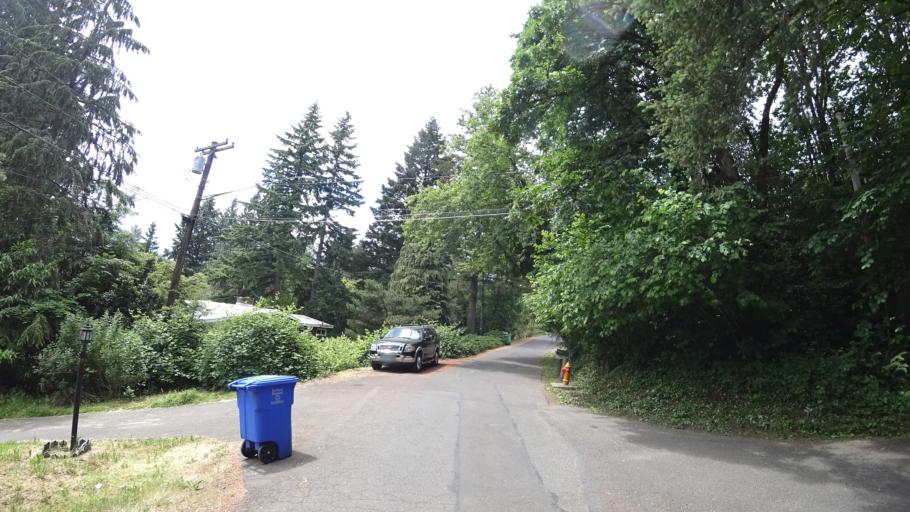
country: US
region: Oregon
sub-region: Clackamas County
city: Lake Oswego
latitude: 45.4496
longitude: -122.6965
